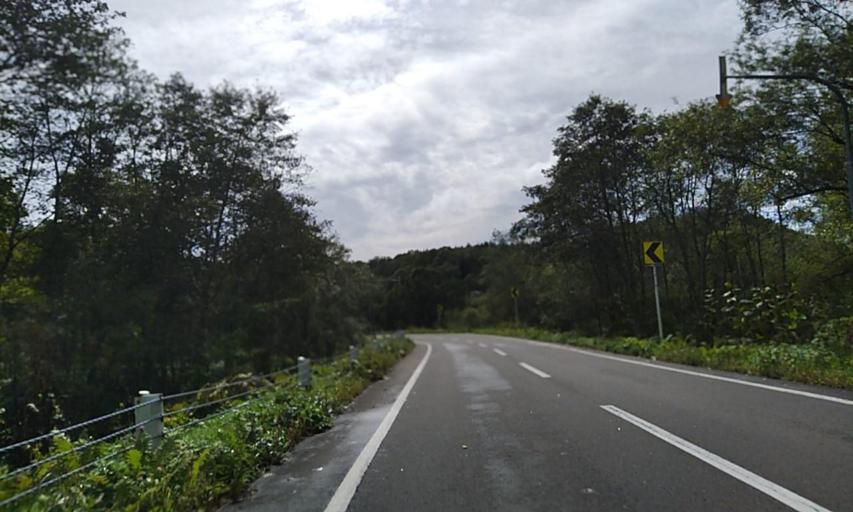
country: JP
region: Hokkaido
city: Kushiro
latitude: 42.8416
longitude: 143.8408
